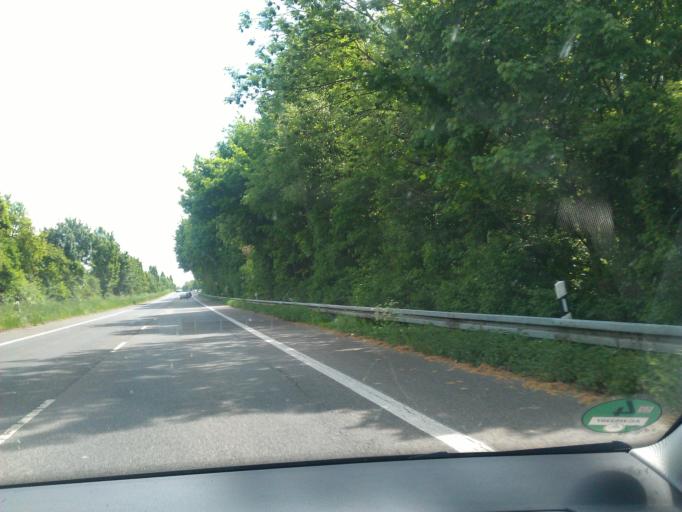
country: DE
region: North Rhine-Westphalia
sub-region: Regierungsbezirk Dusseldorf
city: Hilden
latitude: 51.1789
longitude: 6.9476
